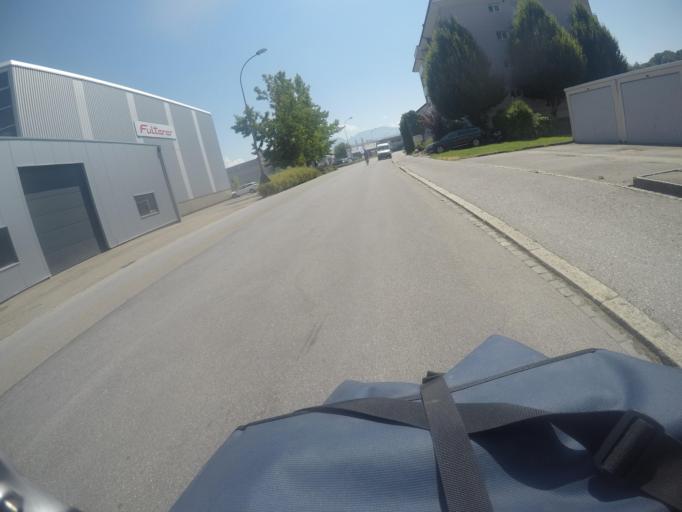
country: CH
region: Saint Gallen
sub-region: Wahlkreis Rheintal
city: Sankt Margrethen
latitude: 47.4482
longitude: 9.6485
